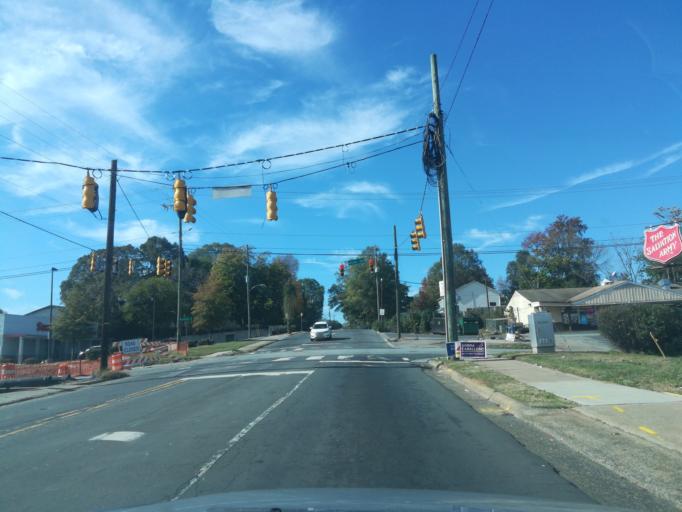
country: US
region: North Carolina
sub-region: Durham County
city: Durham
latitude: 35.9928
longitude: -78.8857
